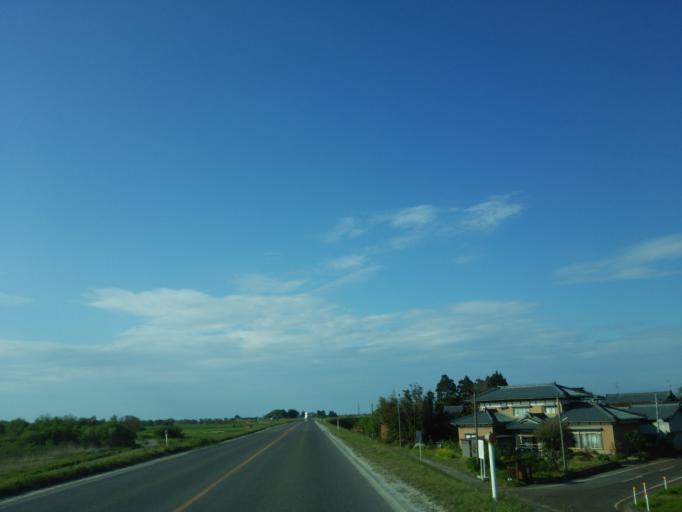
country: JP
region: Niigata
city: Gosen
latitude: 37.7906
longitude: 139.1839
